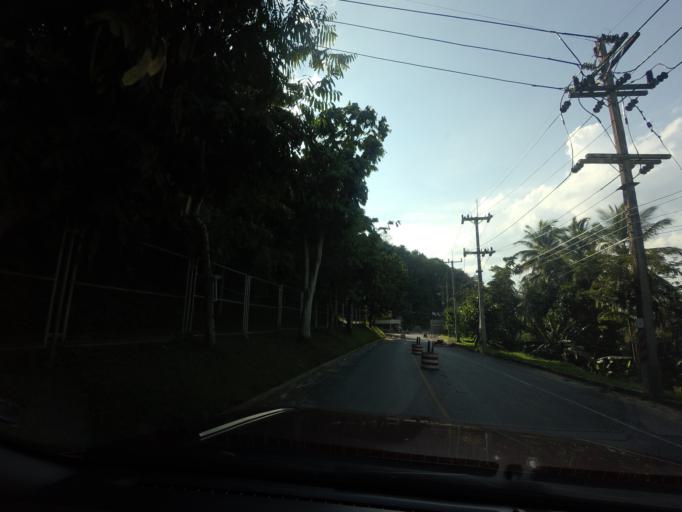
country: TH
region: Yala
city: Than To
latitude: 6.1620
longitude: 101.2695
